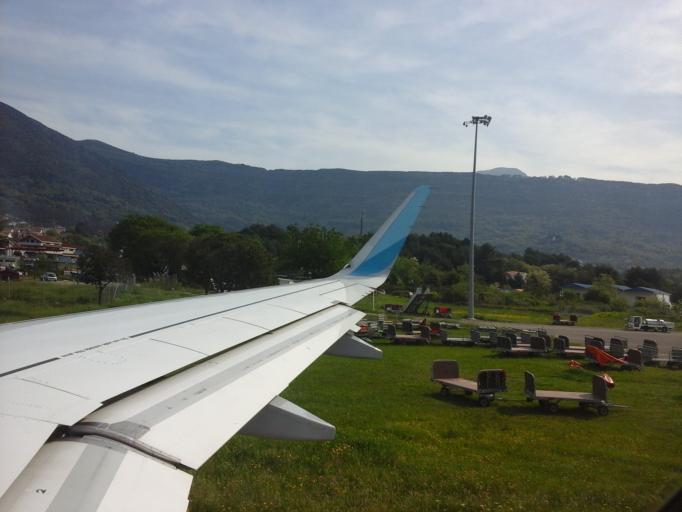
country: ME
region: Tivat
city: Tivat
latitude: 42.4133
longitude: 18.7146
